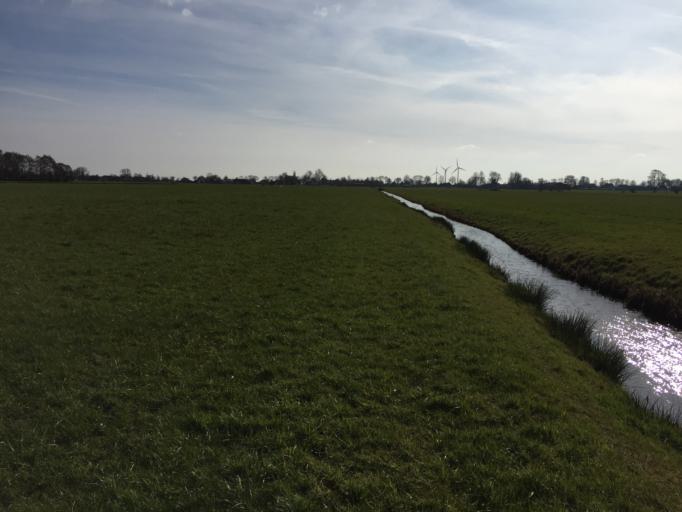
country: NL
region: Utrecht
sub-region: Gemeente Montfoort
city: Montfoort
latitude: 52.0132
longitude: 4.9530
